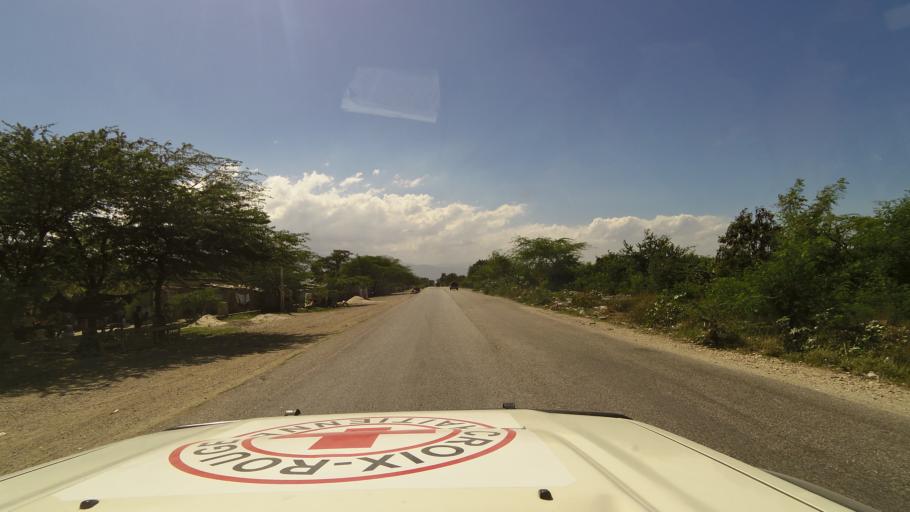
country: HT
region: Ouest
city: Delmas 73
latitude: 18.6368
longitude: -72.3037
